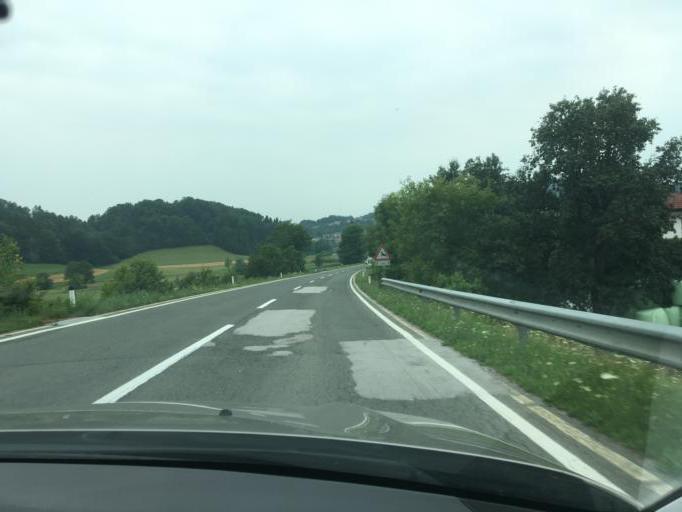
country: SI
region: Skofljica
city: Skofljica
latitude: 45.9804
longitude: 14.5942
